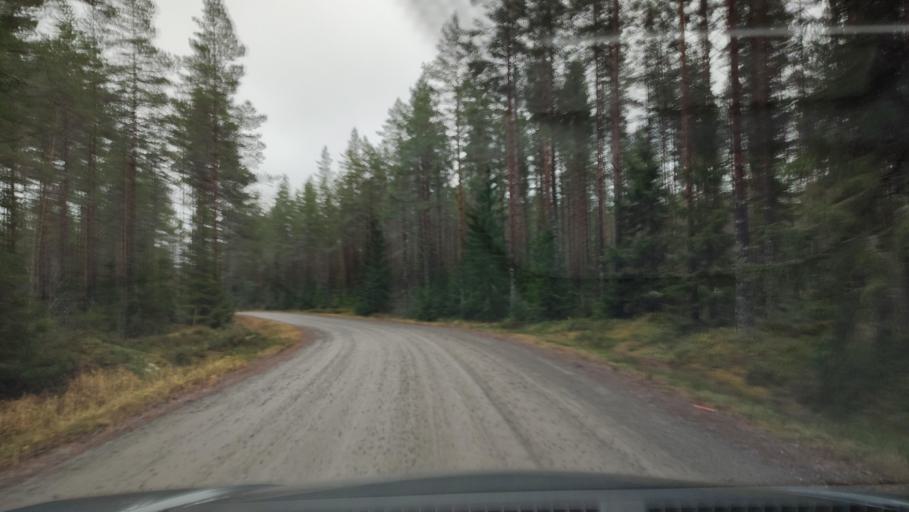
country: FI
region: Southern Ostrobothnia
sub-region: Suupohja
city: Karijoki
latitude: 62.1379
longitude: 21.6576
